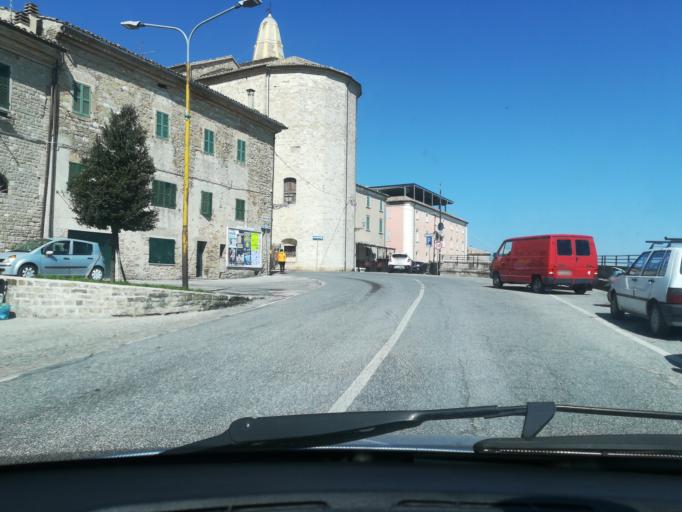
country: IT
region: The Marches
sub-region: Provincia di Macerata
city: Cingoli
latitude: 43.3754
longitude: 13.2175
